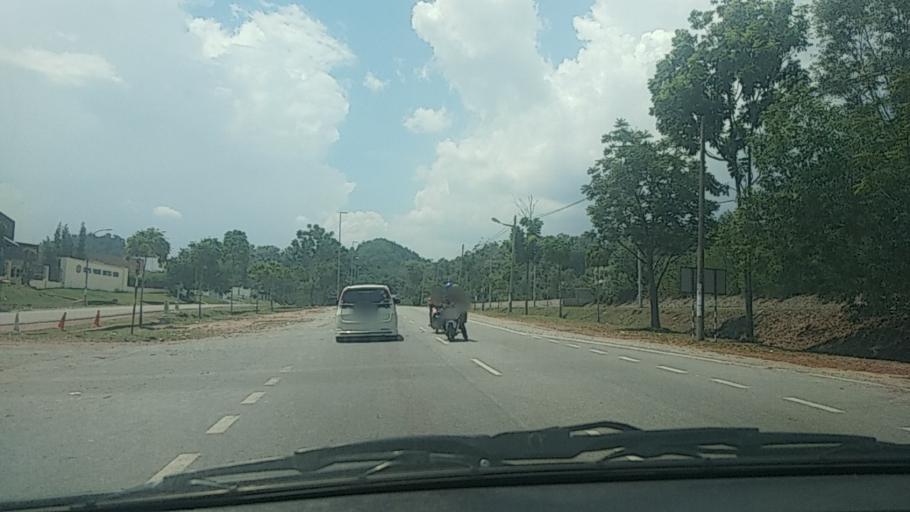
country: MY
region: Kedah
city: Sungai Petani
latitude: 5.6465
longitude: 100.5358
